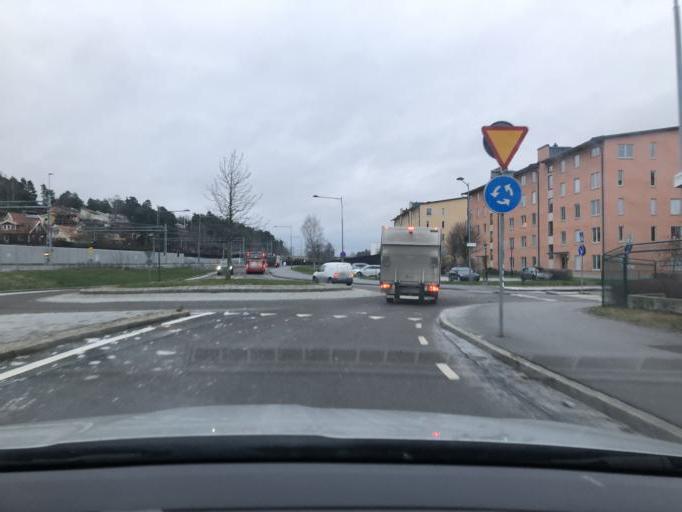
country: SE
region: Stockholm
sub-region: Stockholms Kommun
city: Kista
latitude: 59.3863
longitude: 17.8915
